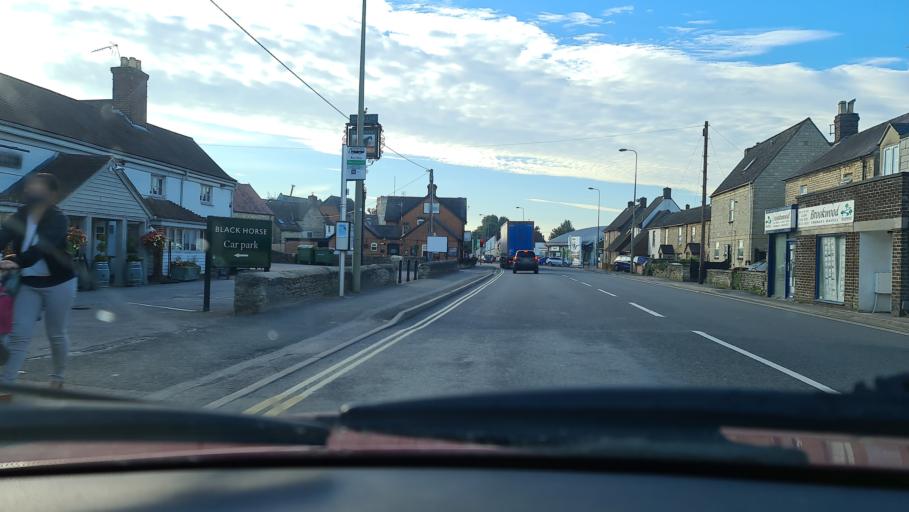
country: GB
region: England
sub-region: Oxfordshire
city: Kidlington
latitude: 51.8238
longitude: -1.2917
